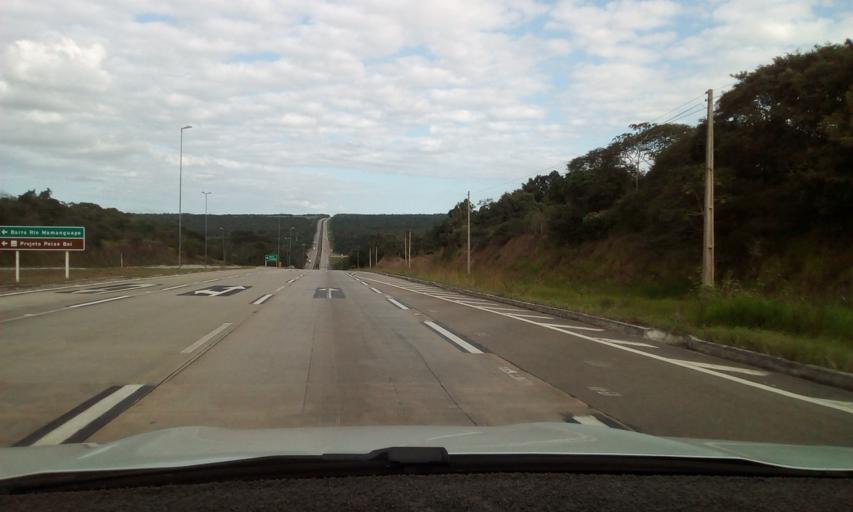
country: BR
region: Paraiba
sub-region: Mamanguape
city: Mamanguape
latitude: -6.9329
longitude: -35.1026
